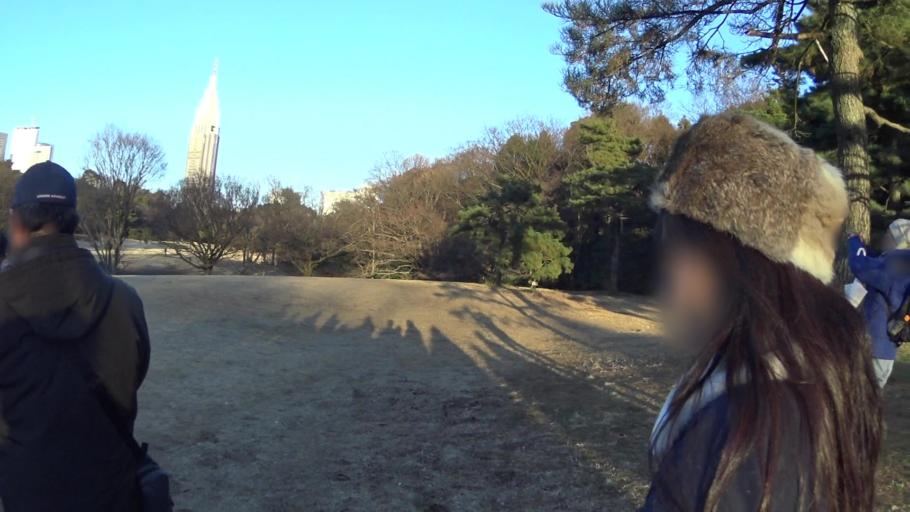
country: JP
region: Tokyo
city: Tokyo
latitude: 35.6780
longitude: 139.6975
